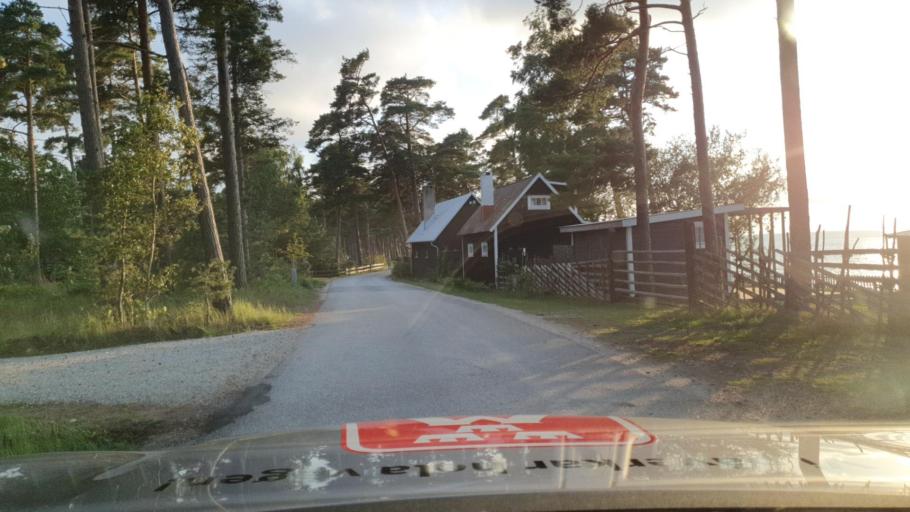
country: SE
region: Gotland
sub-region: Gotland
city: Klintehamn
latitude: 57.3146
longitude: 18.1611
